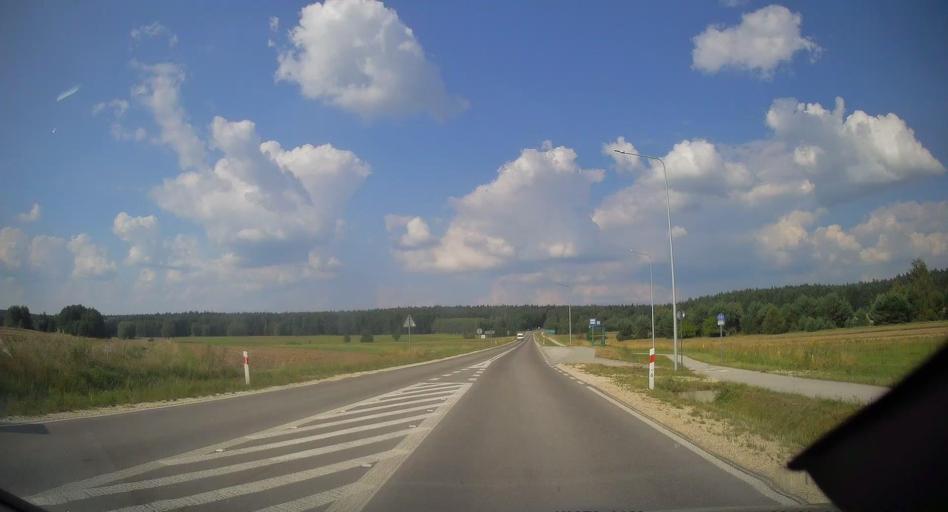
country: PL
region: Swietokrzyskie
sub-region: Powiat kielecki
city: Lopuszno
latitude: 51.0002
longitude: 20.2700
